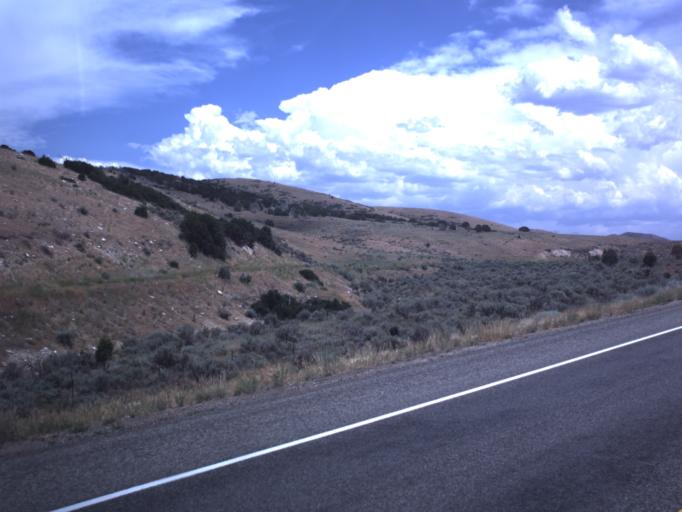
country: US
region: Utah
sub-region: Sanpete County
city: Fountain Green
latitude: 39.6971
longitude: -111.6947
